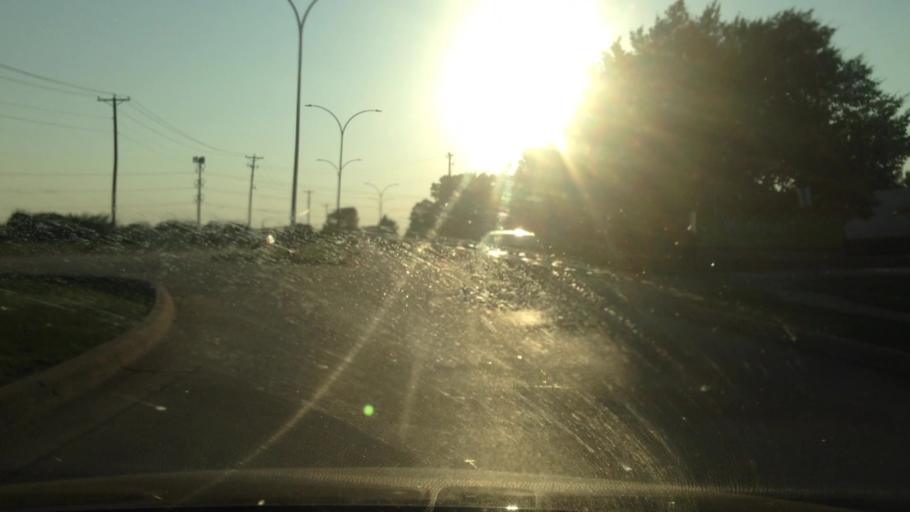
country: US
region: Texas
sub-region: Tarrant County
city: Dalworthington Gardens
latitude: 32.6450
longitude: -97.1169
